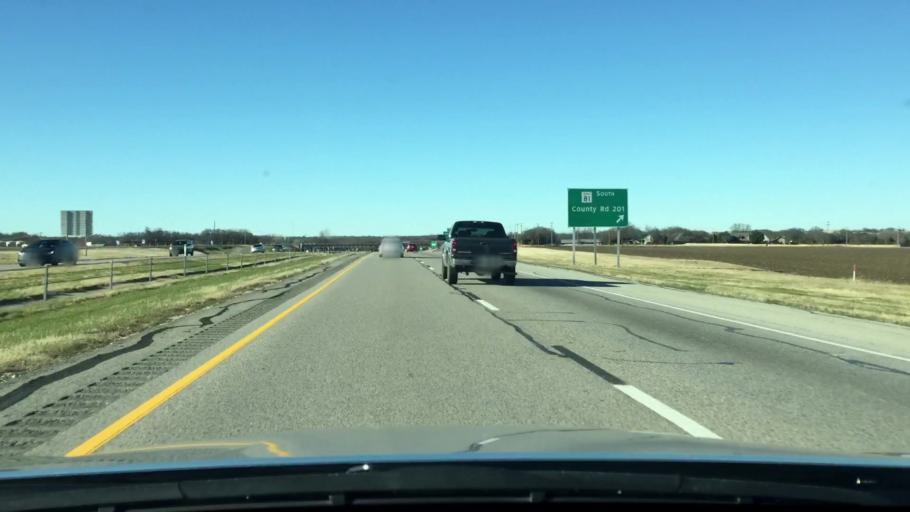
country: US
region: Texas
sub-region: Johnson County
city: Grandview
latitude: 32.2827
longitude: -97.1754
